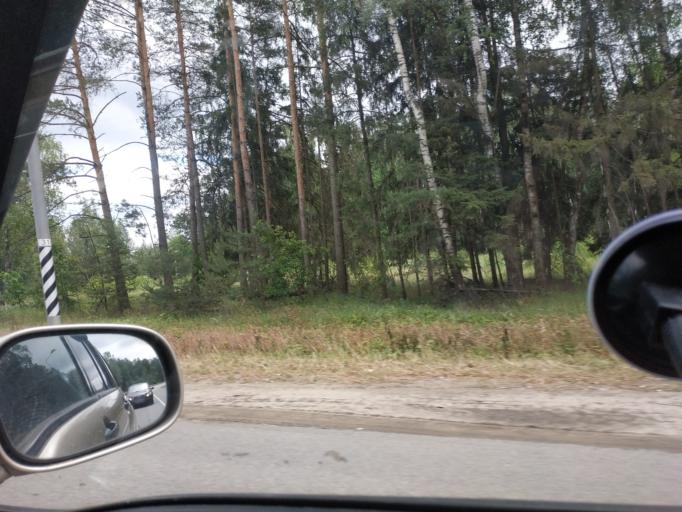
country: RU
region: Moskovskaya
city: Krasnoarmeysk
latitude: 56.0175
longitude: 38.1596
